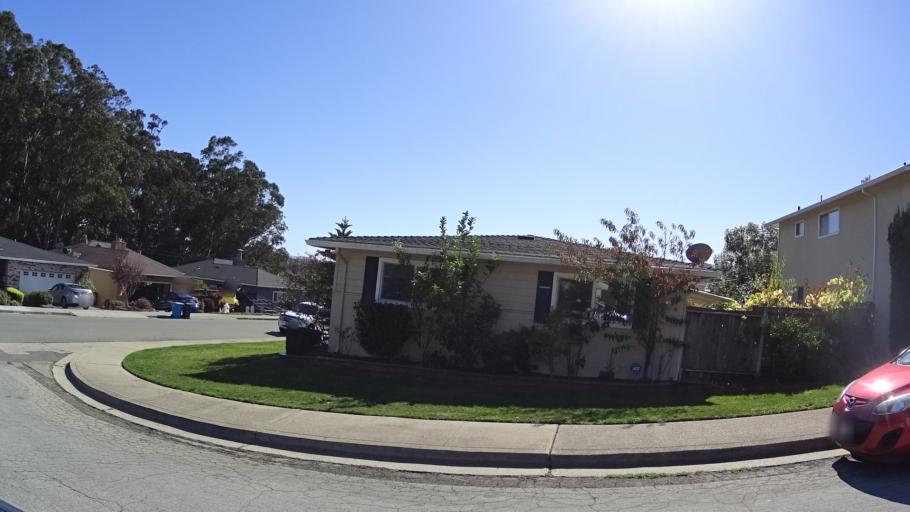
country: US
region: California
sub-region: San Mateo County
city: San Bruno
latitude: 37.6218
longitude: -122.4313
